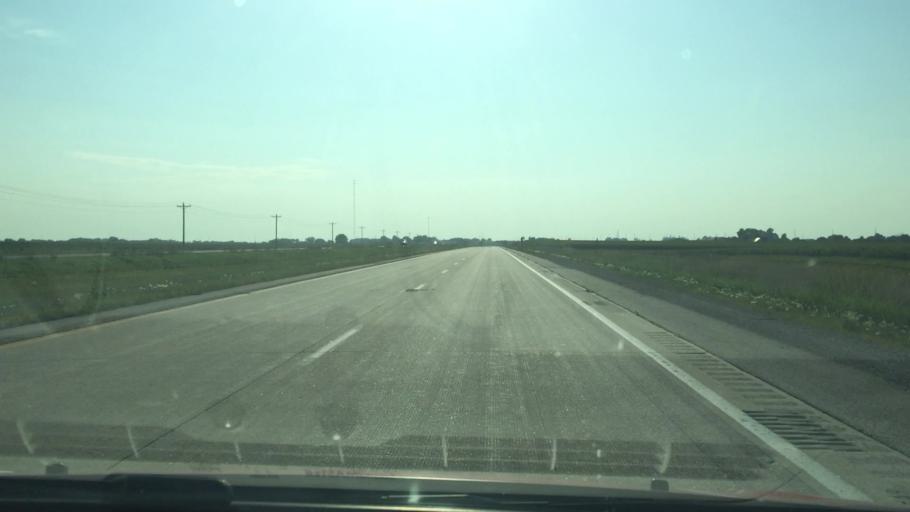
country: US
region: Iowa
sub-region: Cedar County
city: Durant
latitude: 41.5197
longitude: -90.8619
